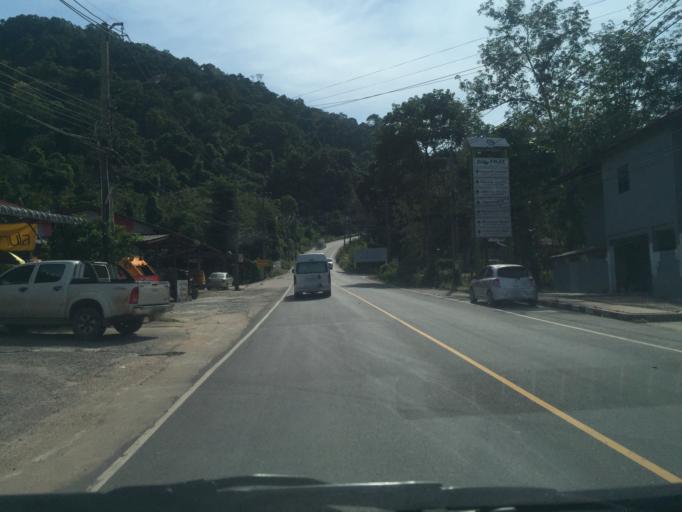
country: TH
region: Trat
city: Laem Ngop
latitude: 12.1280
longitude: 102.2717
